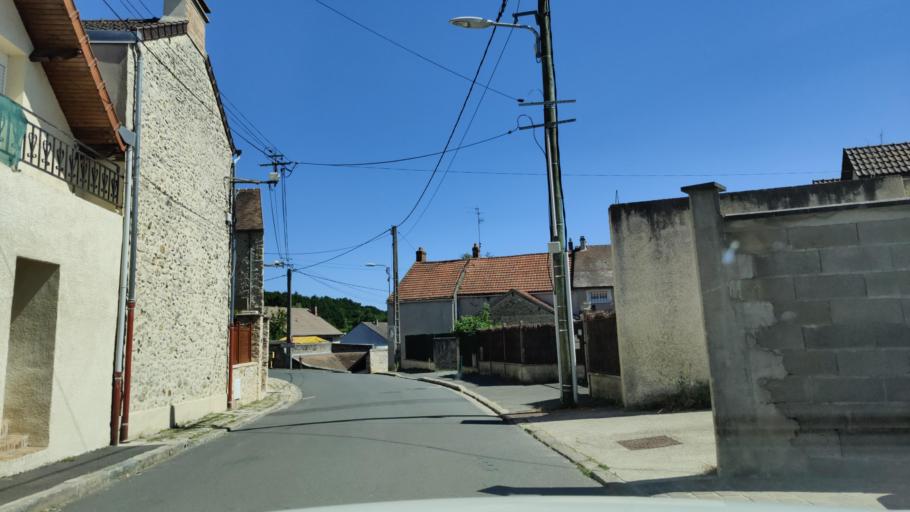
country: FR
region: Ile-de-France
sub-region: Departement de l'Essonne
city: Bruyeres-le-Chatel
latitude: 48.5955
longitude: 2.1756
